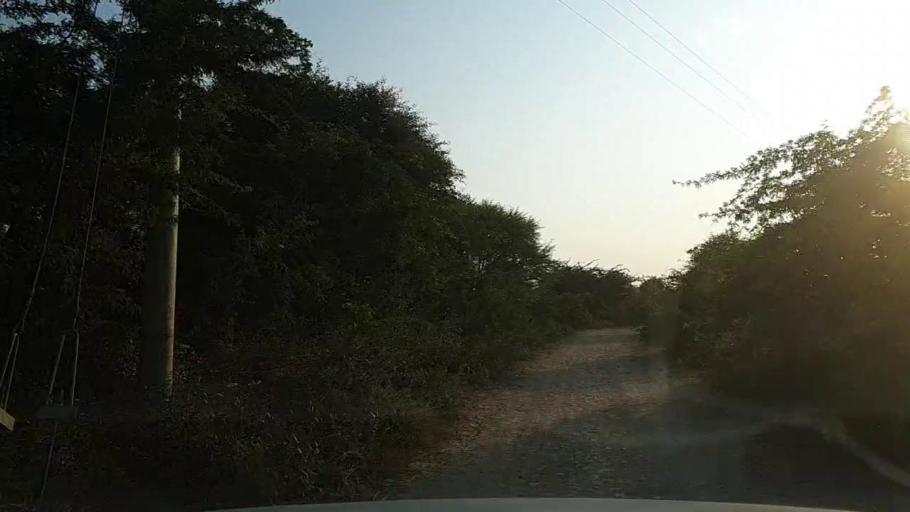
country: PK
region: Sindh
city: Daro Mehar
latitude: 24.7463
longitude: 68.1849
